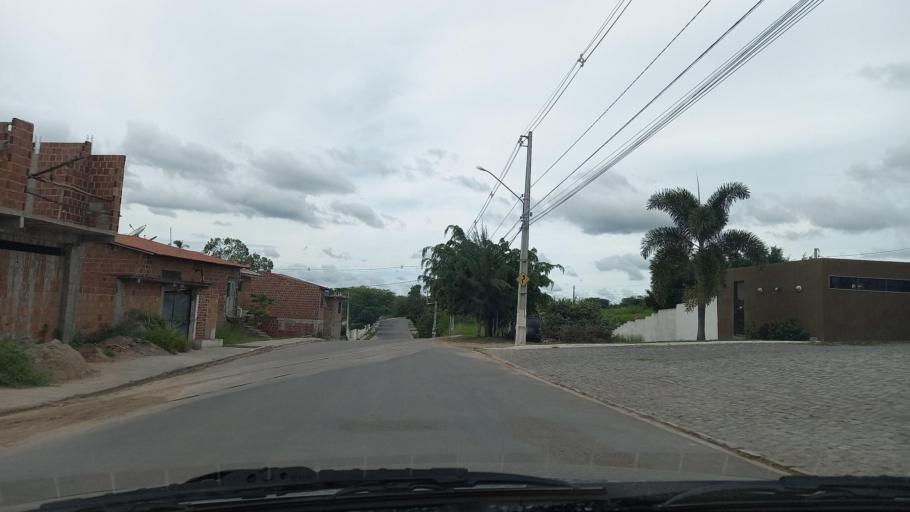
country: BR
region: Pernambuco
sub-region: Gravata
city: Gravata
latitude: -8.2112
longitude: -35.5988
